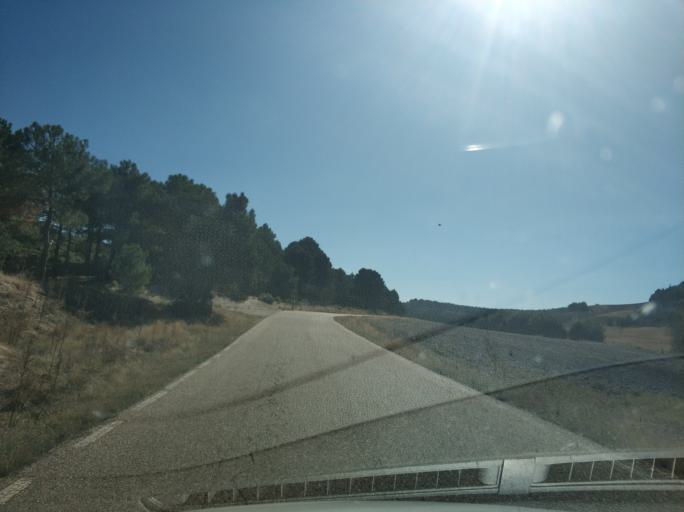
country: ES
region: Castille and Leon
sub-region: Provincia de Soria
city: Espeja de San Marcelino
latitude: 41.7846
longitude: -3.1945
